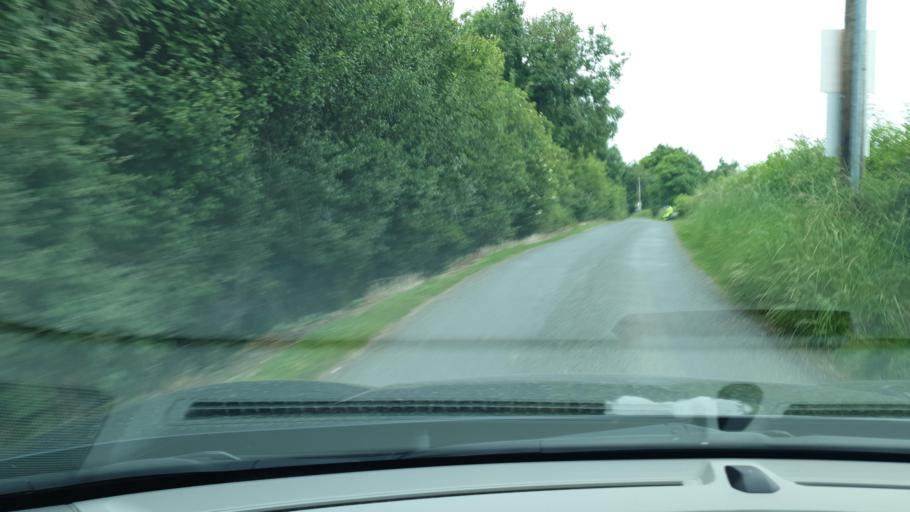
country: IE
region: Leinster
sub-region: An Mhi
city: Ashbourne
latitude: 53.4793
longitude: -6.3814
